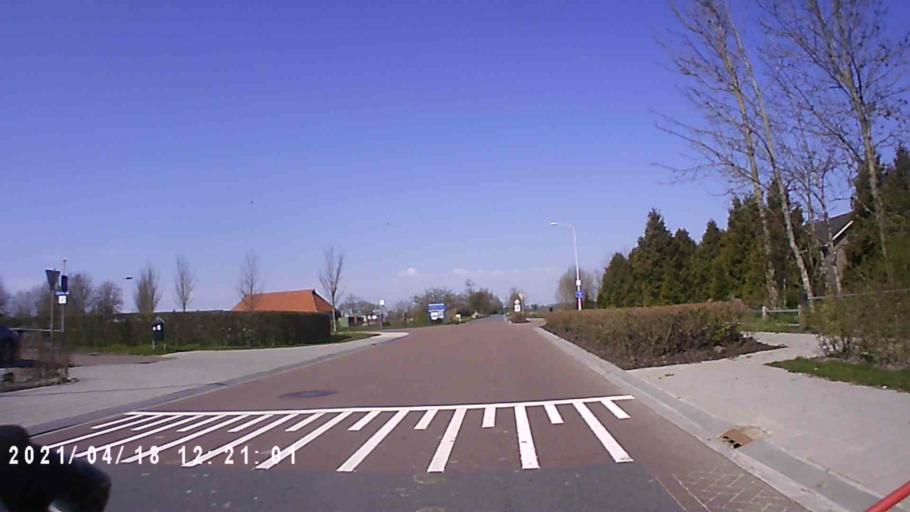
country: NL
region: Friesland
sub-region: Gemeente Kollumerland en Nieuwkruisland
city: Kollum
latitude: 53.3213
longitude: 6.1365
